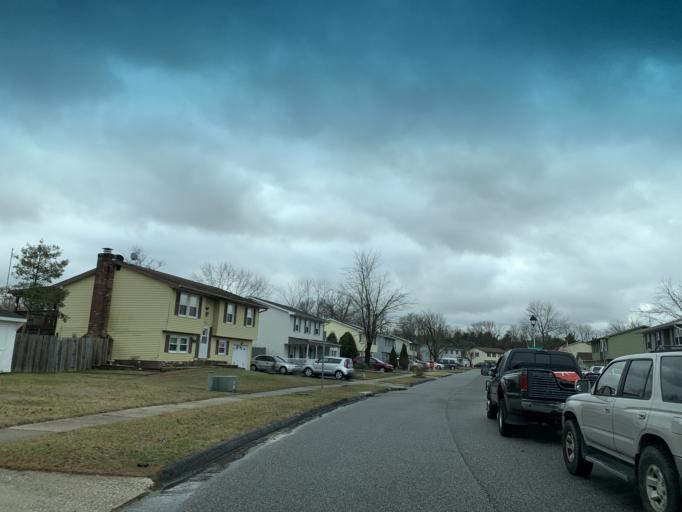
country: US
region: Maryland
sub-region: Harford County
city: Edgewood
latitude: 39.4280
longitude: -76.3137
